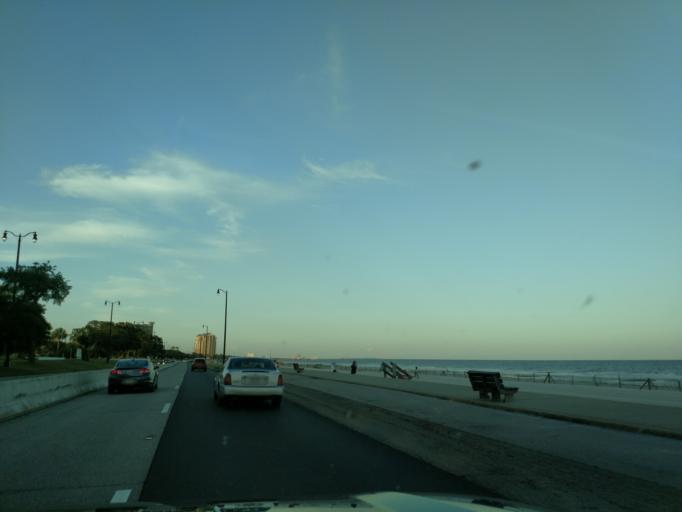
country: US
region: Mississippi
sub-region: Harrison County
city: Gulfport
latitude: 30.3857
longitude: -89.0119
